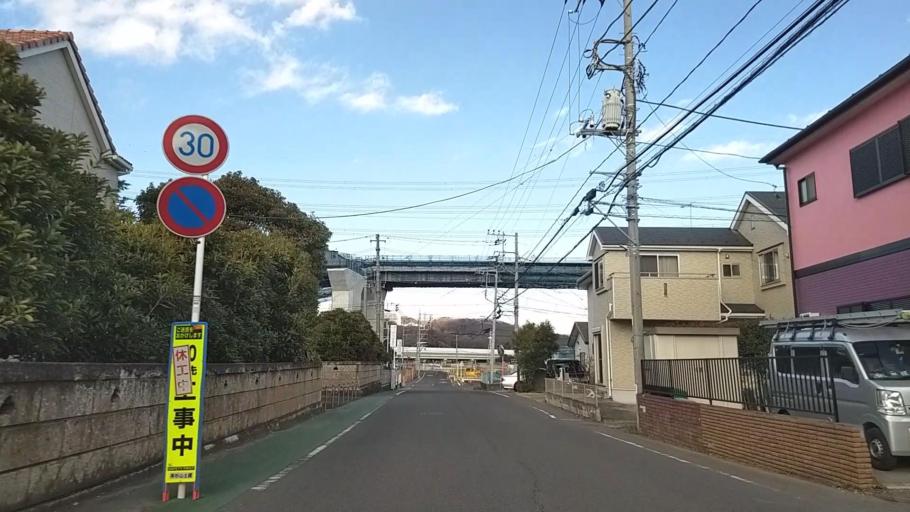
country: JP
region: Kanagawa
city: Isehara
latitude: 35.4081
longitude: 139.3180
